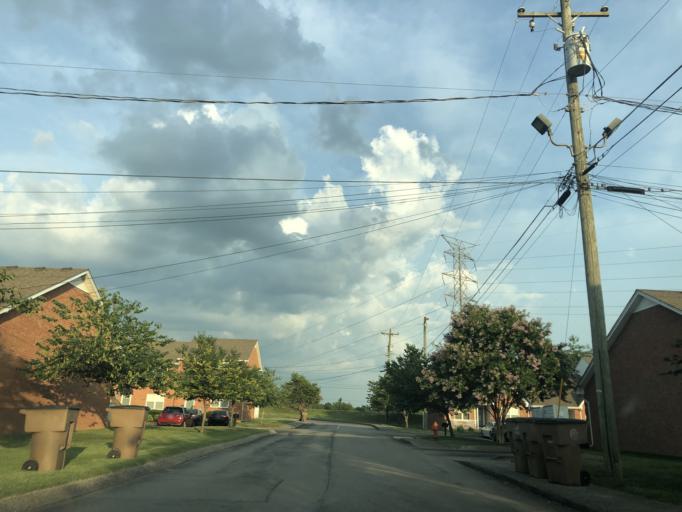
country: US
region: Tennessee
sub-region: Davidson County
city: Nashville
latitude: 36.1638
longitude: -86.7013
